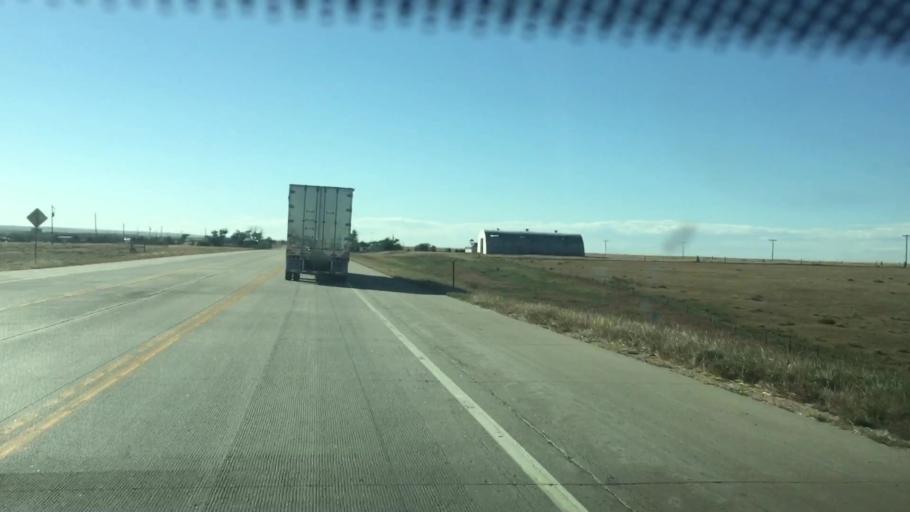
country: US
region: Colorado
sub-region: Kiowa County
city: Eads
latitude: 38.8255
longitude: -102.9996
